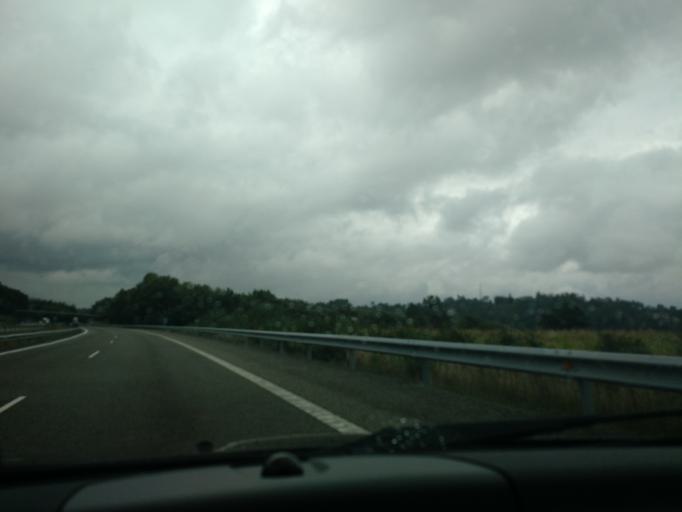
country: ES
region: Galicia
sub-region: Provincia da Coruna
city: Santiago de Compostela
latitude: 42.9166
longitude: -8.4771
